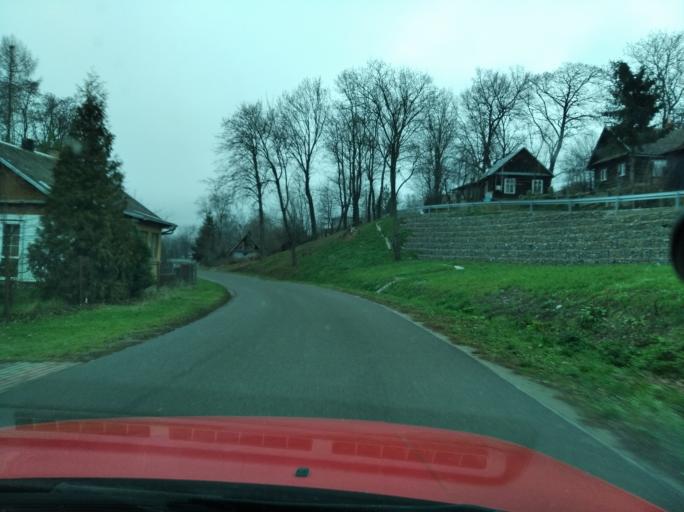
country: PL
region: Subcarpathian Voivodeship
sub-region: Powiat przeworski
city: Rozborz
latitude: 50.0578
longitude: 22.5456
